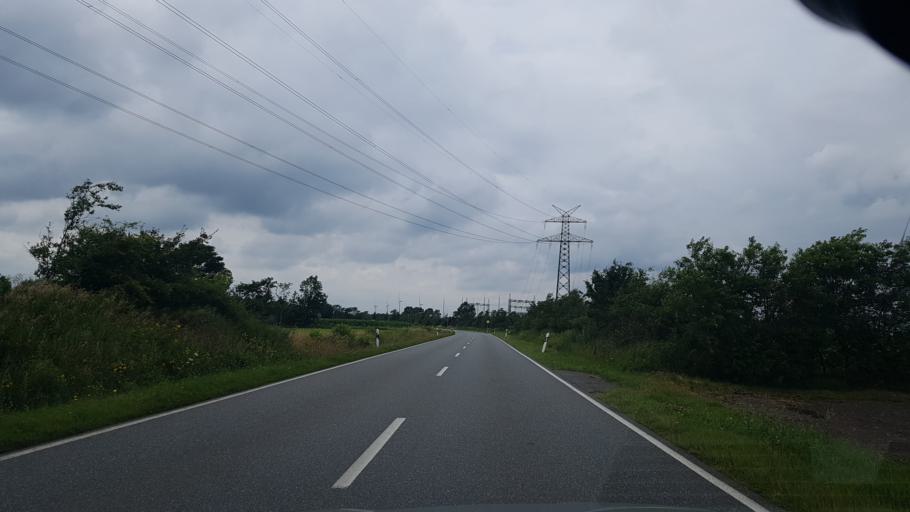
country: DE
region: Schleswig-Holstein
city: Jardelund
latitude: 54.8466
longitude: 9.2021
